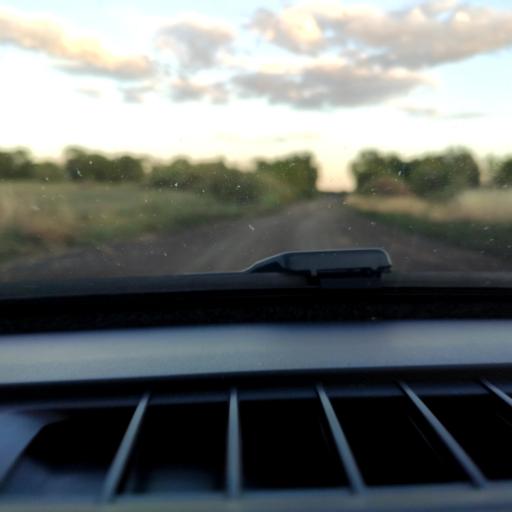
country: RU
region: Voronezj
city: Verkhnyaya Khava
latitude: 51.6079
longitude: 39.8355
